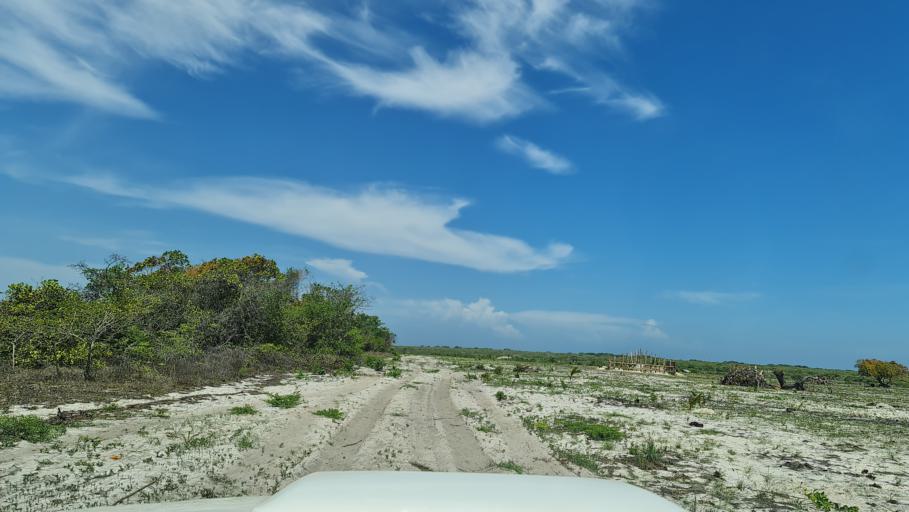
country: MZ
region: Nampula
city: Ilha de Mocambique
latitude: -15.1960
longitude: 40.6169
